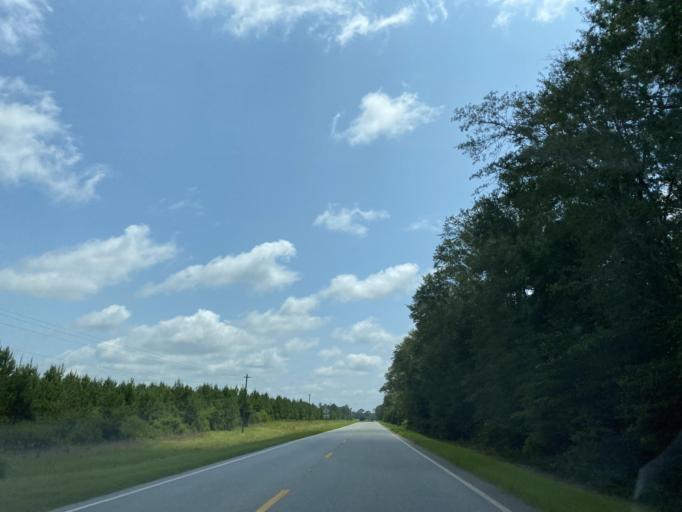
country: US
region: Georgia
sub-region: Telfair County
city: Helena
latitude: 32.0296
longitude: -83.0211
